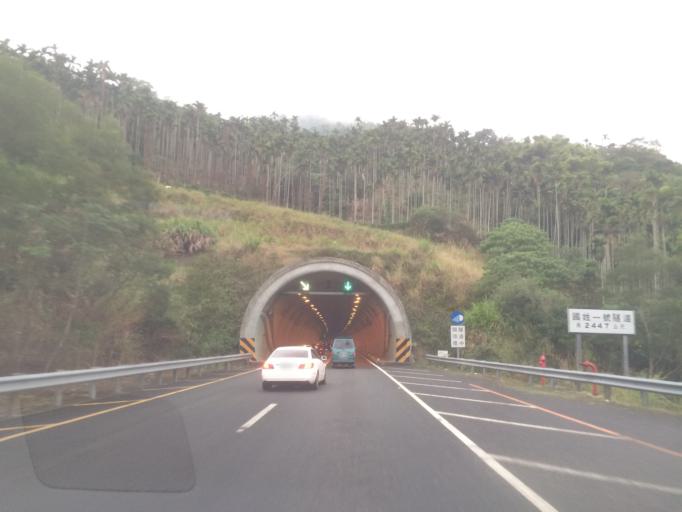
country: TW
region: Taiwan
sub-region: Nantou
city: Puli
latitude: 24.0005
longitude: 120.8431
